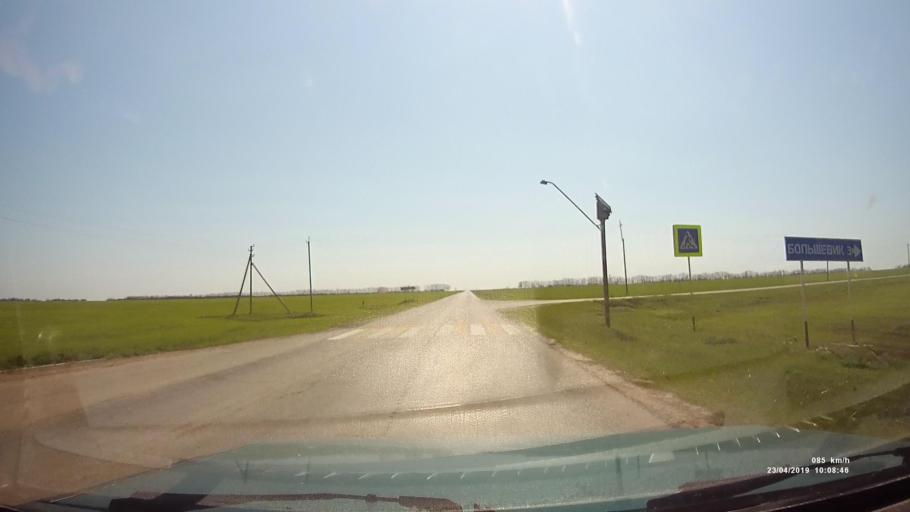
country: RU
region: Rostov
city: Sovetskoye
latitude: 46.7172
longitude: 42.2700
